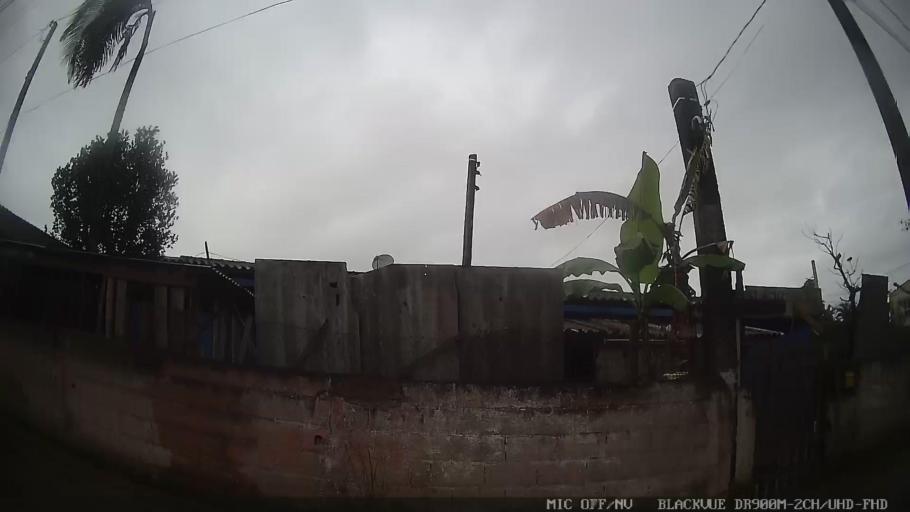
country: BR
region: Sao Paulo
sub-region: Itanhaem
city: Itanhaem
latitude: -24.1842
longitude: -46.8155
